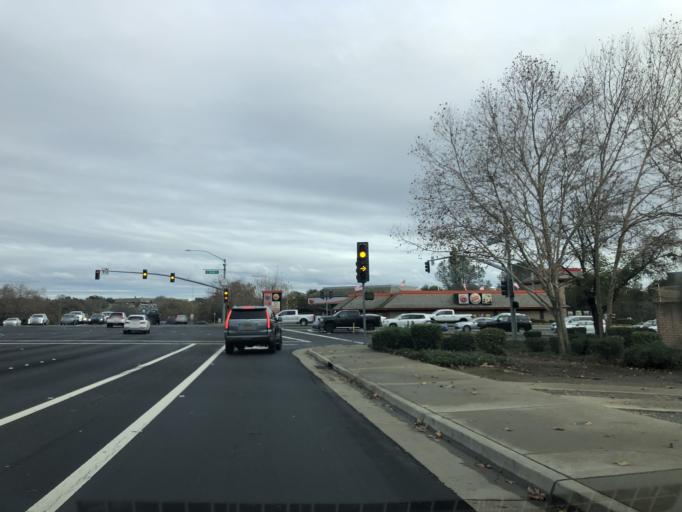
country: US
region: California
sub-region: Placer County
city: Roseville
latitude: 38.7621
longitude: -121.2567
